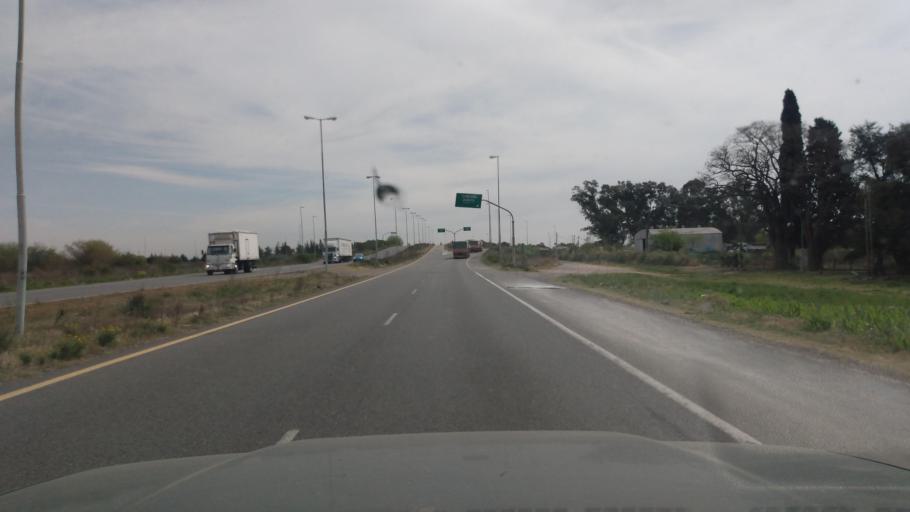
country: AR
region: Buenos Aires
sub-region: Partido de Lujan
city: Lujan
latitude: -34.4737
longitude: -59.0664
